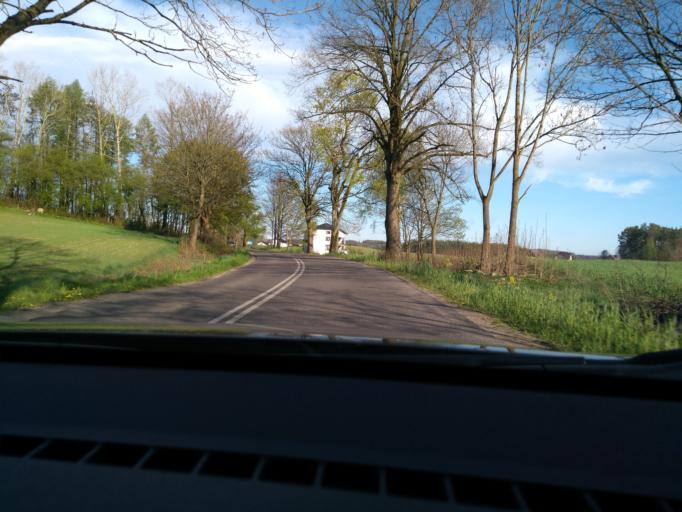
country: PL
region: Pomeranian Voivodeship
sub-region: Powiat kartuski
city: Suleczyno
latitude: 54.3285
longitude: 17.7769
